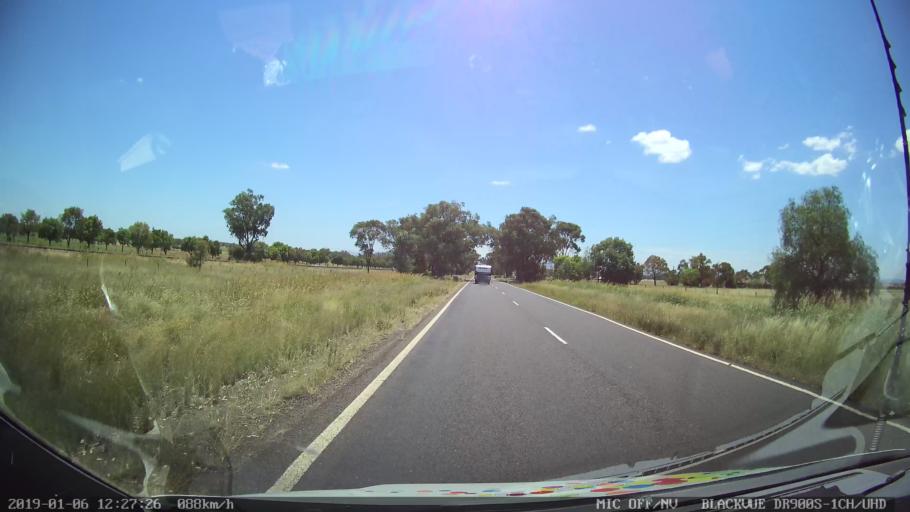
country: AU
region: New South Wales
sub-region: Tamworth Municipality
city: Phillip
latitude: -31.2067
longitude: 150.8280
